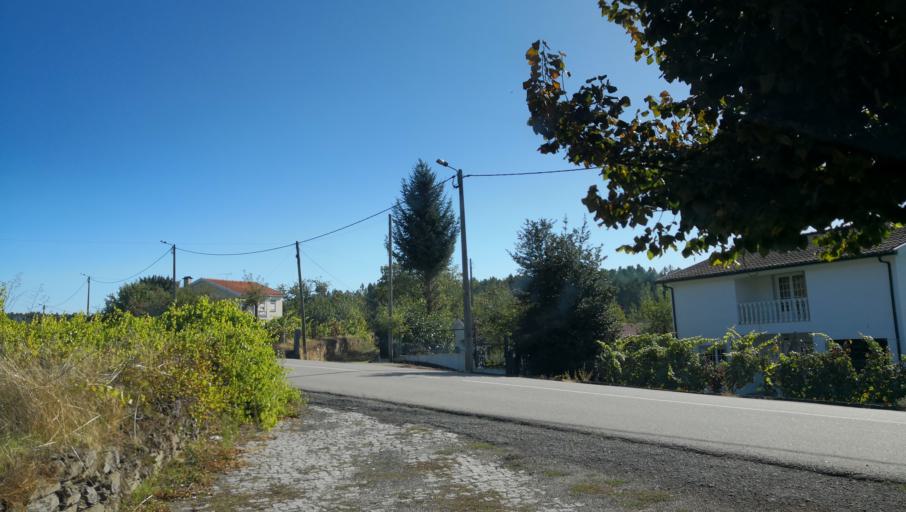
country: PT
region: Vila Real
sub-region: Sabrosa
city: Vilela
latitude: 41.2520
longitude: -7.6346
